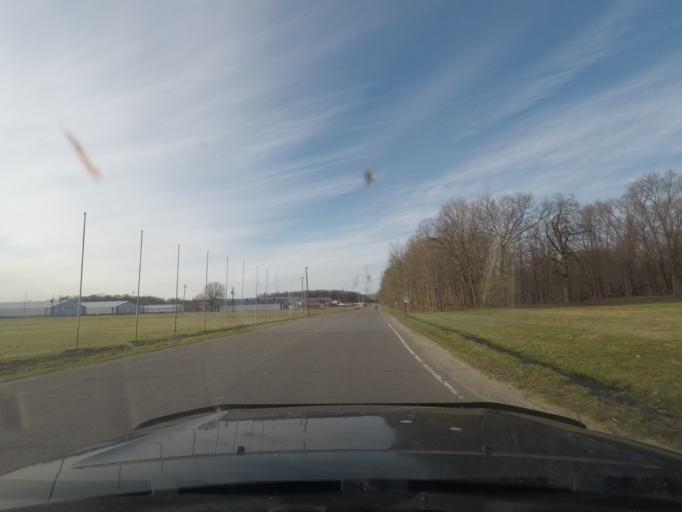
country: US
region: Indiana
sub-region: LaPorte County
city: LaPorte
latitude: 41.5930
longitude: -86.7492
